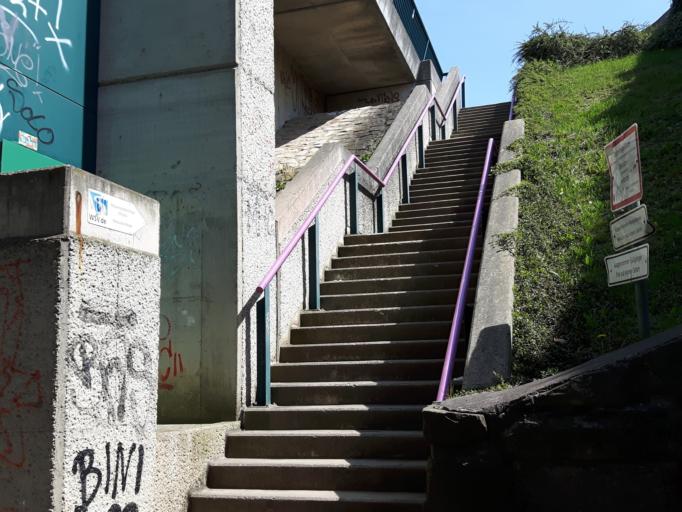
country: DE
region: North Rhine-Westphalia
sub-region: Regierungsbezirk Detmold
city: Minden
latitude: 52.3033
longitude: 8.9320
